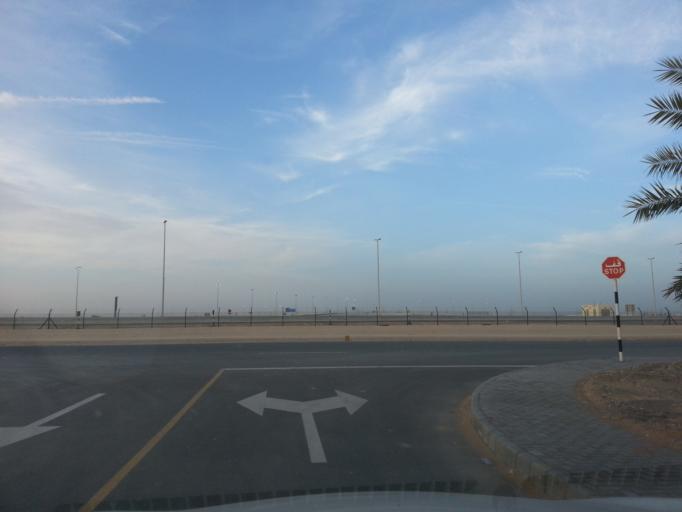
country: AE
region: Abu Dhabi
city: Abu Dhabi
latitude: 24.7809
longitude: 54.7275
